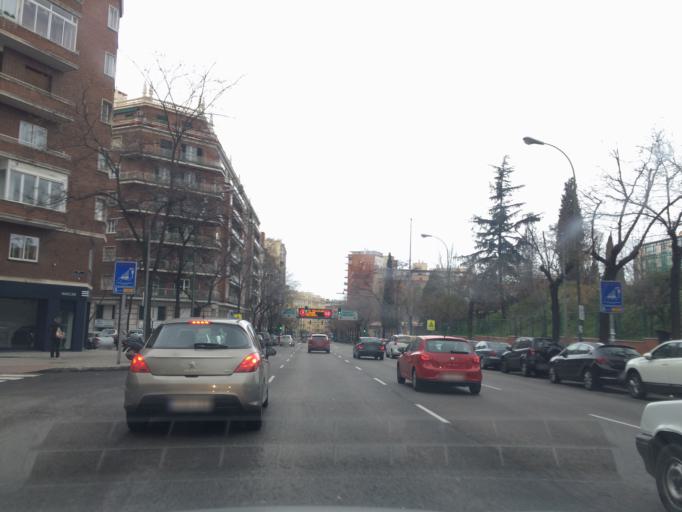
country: ES
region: Madrid
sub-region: Provincia de Madrid
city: Chamberi
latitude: 40.4404
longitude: -3.7093
